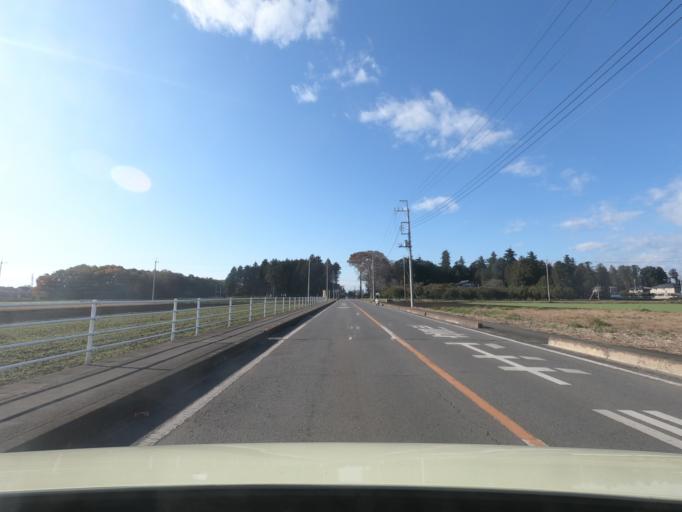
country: JP
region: Ibaraki
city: Koga
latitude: 36.2358
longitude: 139.7608
